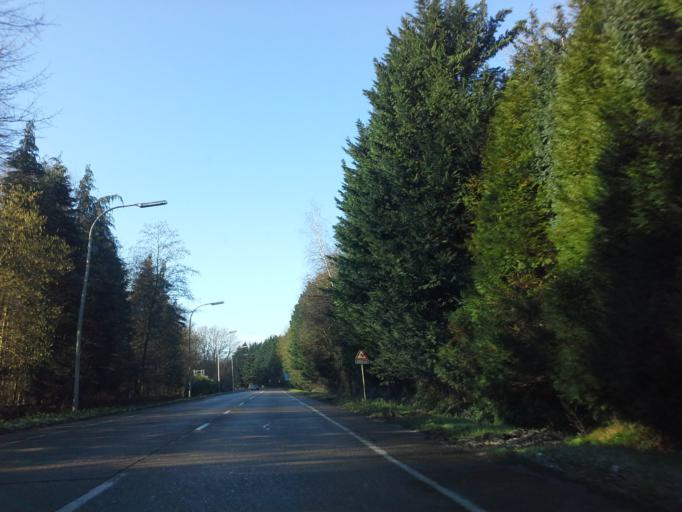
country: BE
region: Flanders
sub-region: Provincie Antwerpen
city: Olen
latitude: 51.1582
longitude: 4.8524
